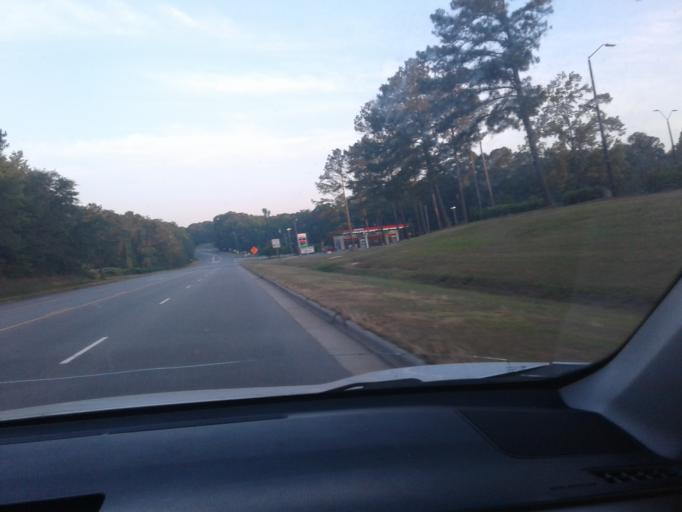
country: US
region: North Carolina
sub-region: Harnett County
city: Buies Creek
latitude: 35.4060
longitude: -78.7436
